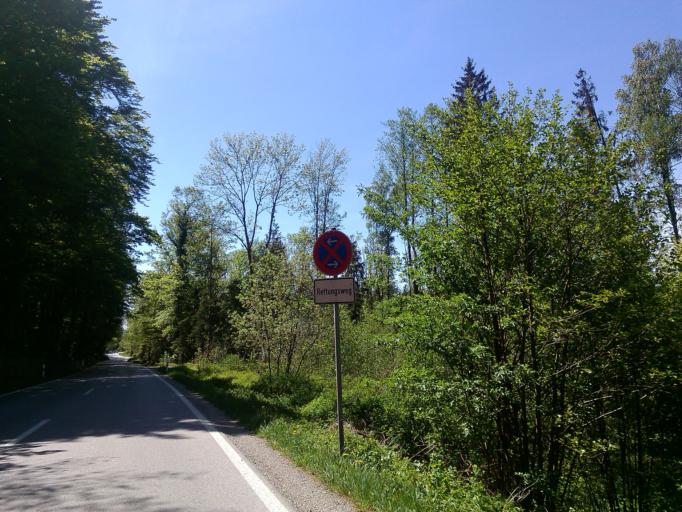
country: DE
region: Bavaria
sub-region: Upper Bavaria
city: Pocking
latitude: 47.9712
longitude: 11.3248
